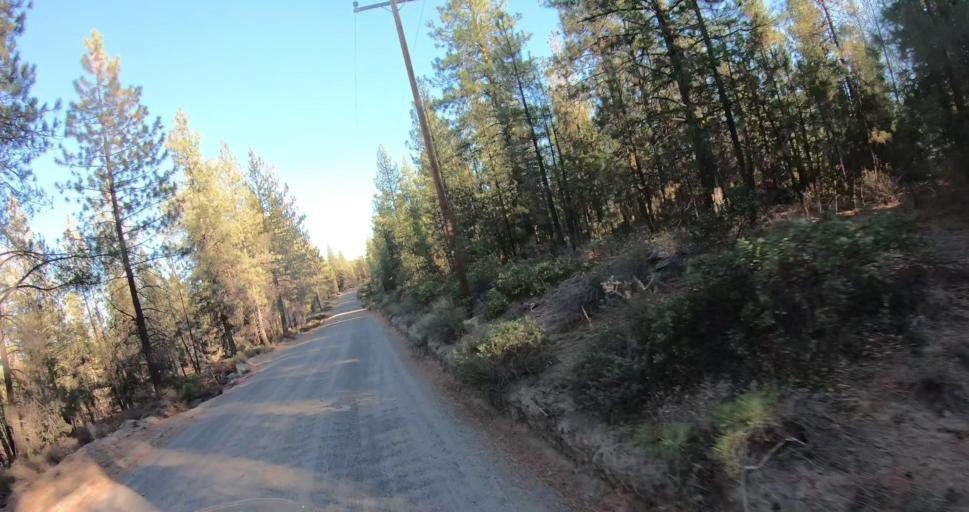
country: US
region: Oregon
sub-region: Deschutes County
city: La Pine
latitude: 43.7202
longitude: -121.3966
